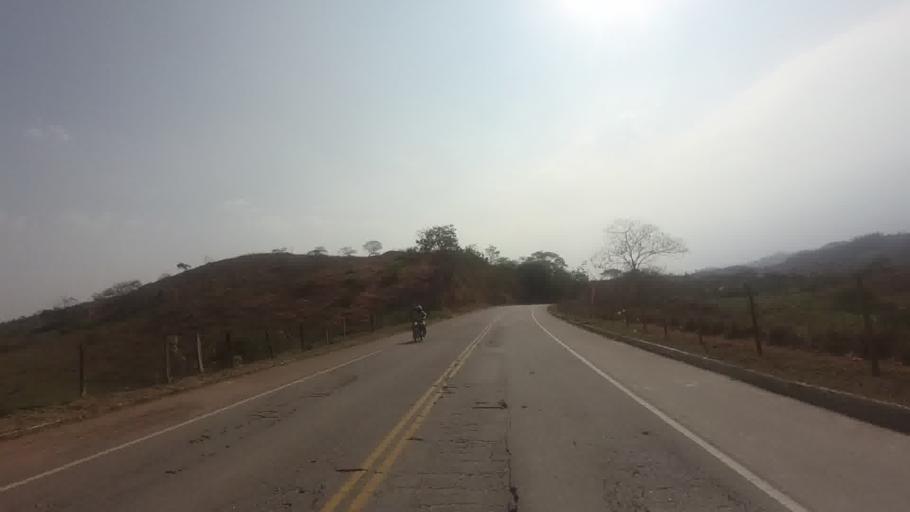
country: BR
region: Rio de Janeiro
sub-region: Bom Jesus Do Itabapoana
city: Bom Jesus do Itabapoana
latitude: -21.1375
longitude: -41.6384
